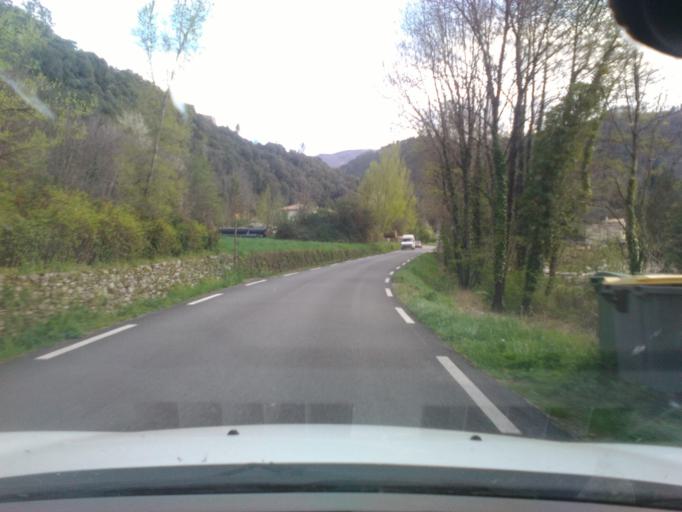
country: FR
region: Languedoc-Roussillon
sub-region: Departement du Gard
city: Lasalle
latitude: 44.1244
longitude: 3.7639
